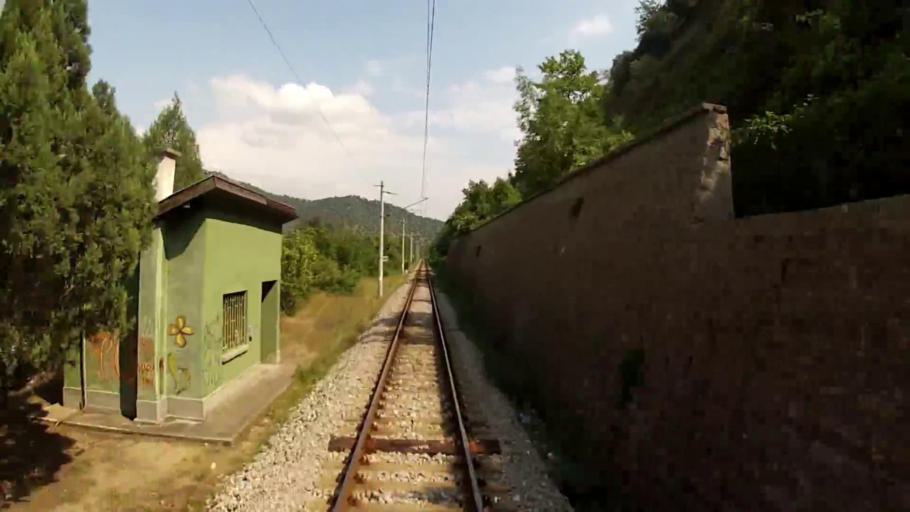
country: BG
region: Blagoevgrad
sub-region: Obshtina Kresna
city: Kresna
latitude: 41.7172
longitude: 23.1691
